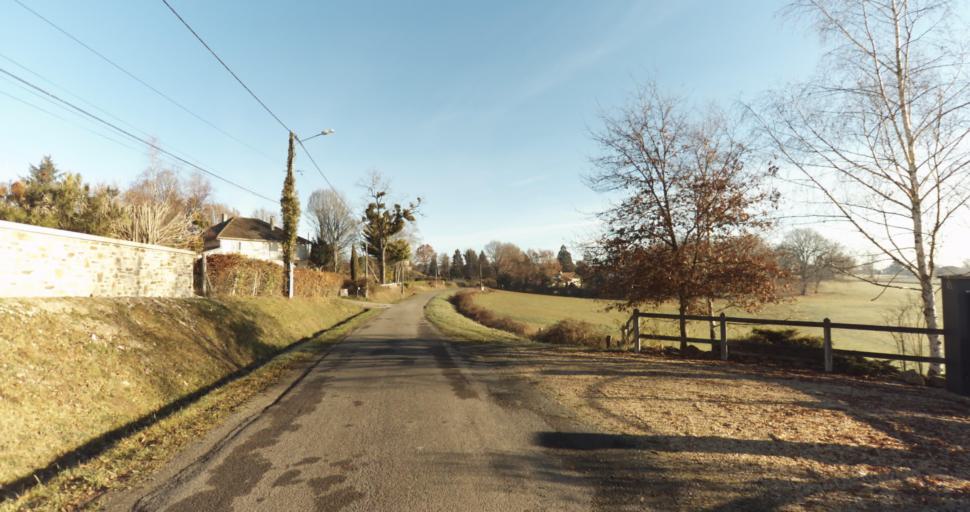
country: FR
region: Limousin
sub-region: Departement de la Haute-Vienne
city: Aixe-sur-Vienne
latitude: 45.8043
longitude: 1.1395
